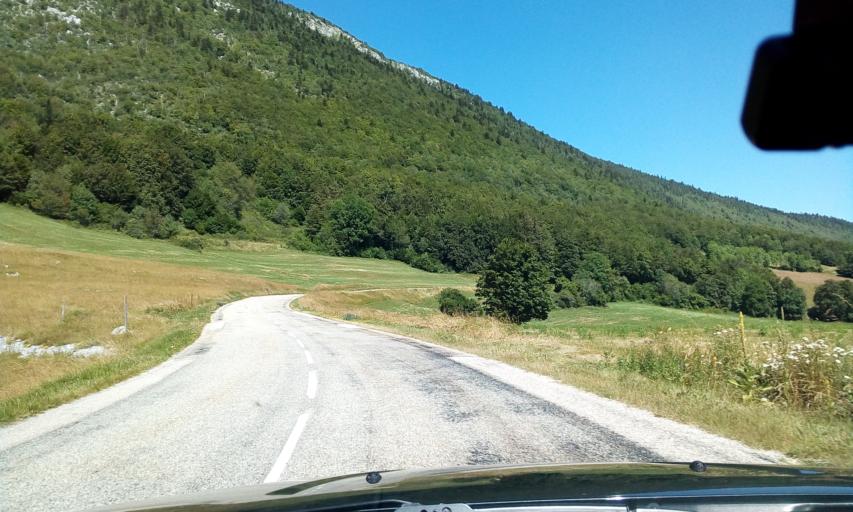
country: FR
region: Rhone-Alpes
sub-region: Departement de la Drome
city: Saint-Laurent-en-Royans
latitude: 44.9237
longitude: 5.3800
